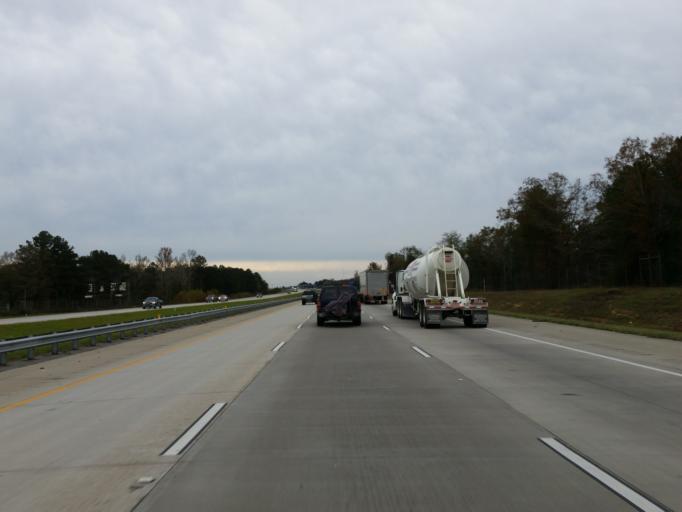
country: US
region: Georgia
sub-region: Dooly County
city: Unadilla
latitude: 32.2240
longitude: -83.7435
